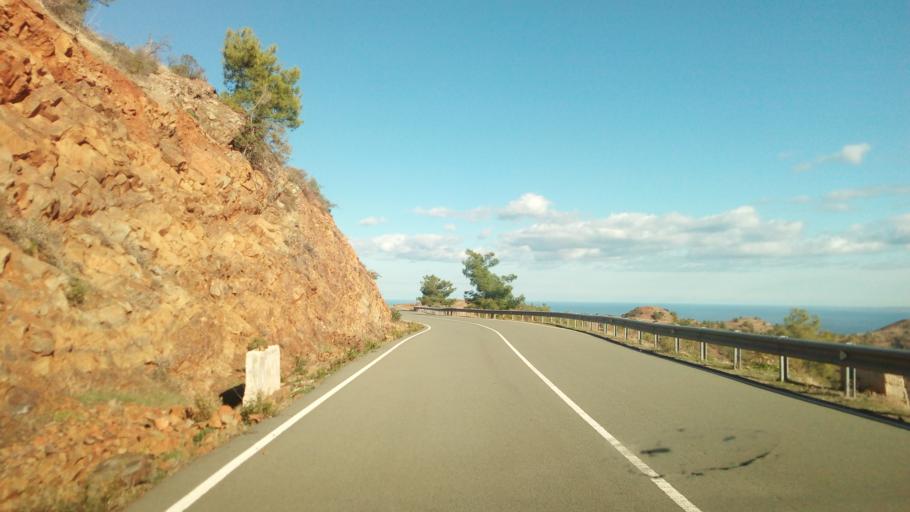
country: CY
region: Lefkosia
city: Lefka
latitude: 35.1035
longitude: 32.7570
